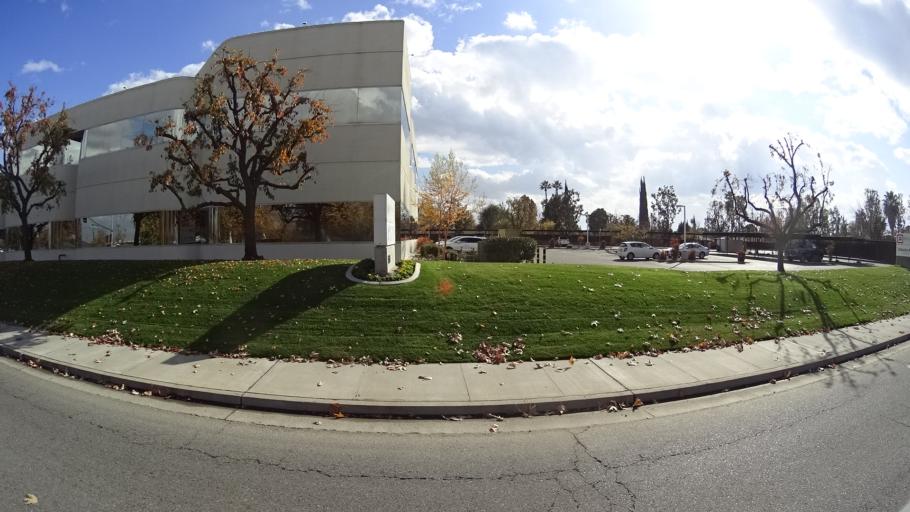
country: US
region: California
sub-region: Kern County
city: Greenacres
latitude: 35.3647
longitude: -119.0663
